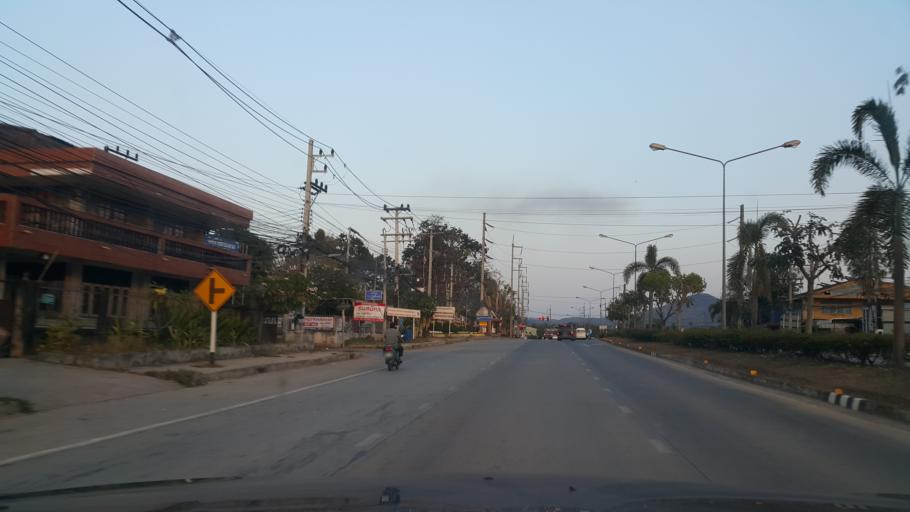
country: TH
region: Loei
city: Loei
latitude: 17.4953
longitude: 101.7186
